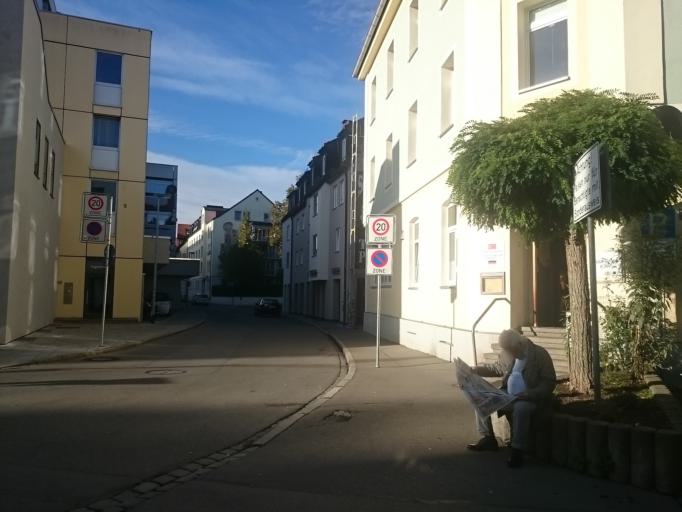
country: DE
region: Bavaria
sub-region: Swabia
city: Kempten (Allgaeu)
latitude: 47.7245
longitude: 10.3179
